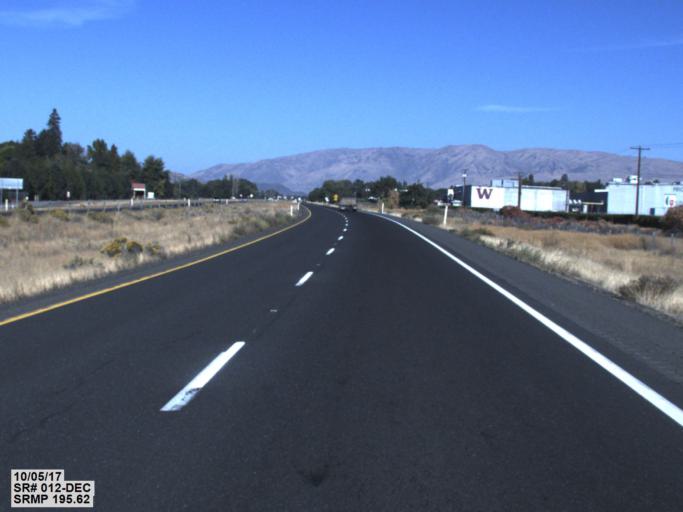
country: US
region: Washington
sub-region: Yakima County
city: Gleed
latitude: 46.6667
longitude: -120.6267
